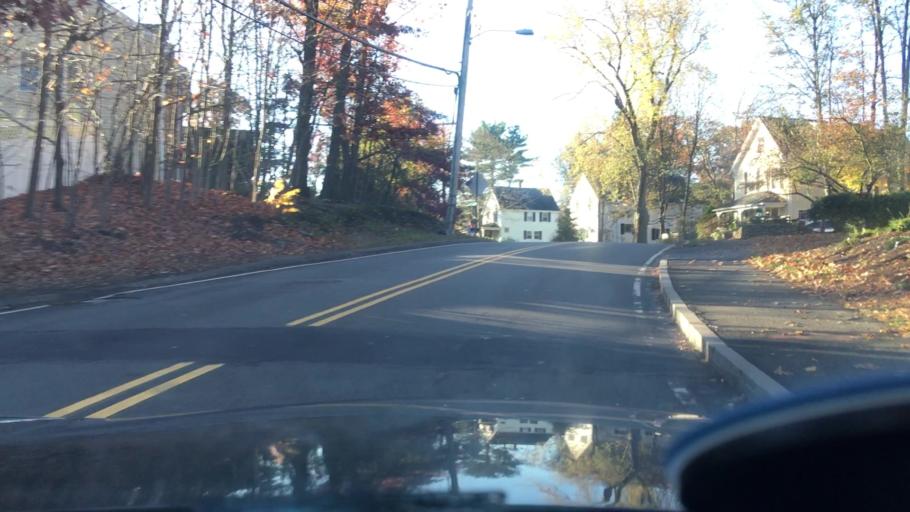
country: US
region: Massachusetts
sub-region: Norfolk County
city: Needham
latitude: 42.3116
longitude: -71.2452
